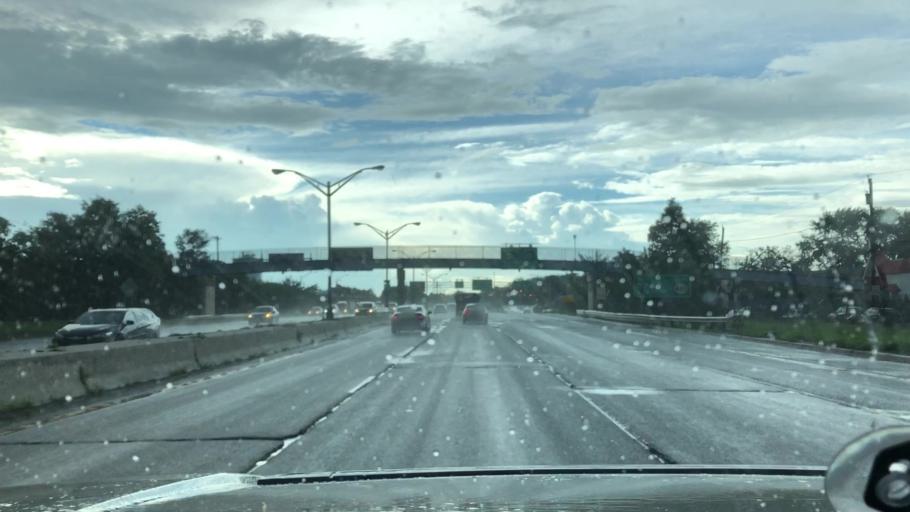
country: US
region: New Jersey
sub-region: Middlesex County
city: Perth Amboy
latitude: 40.5267
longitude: -74.2705
